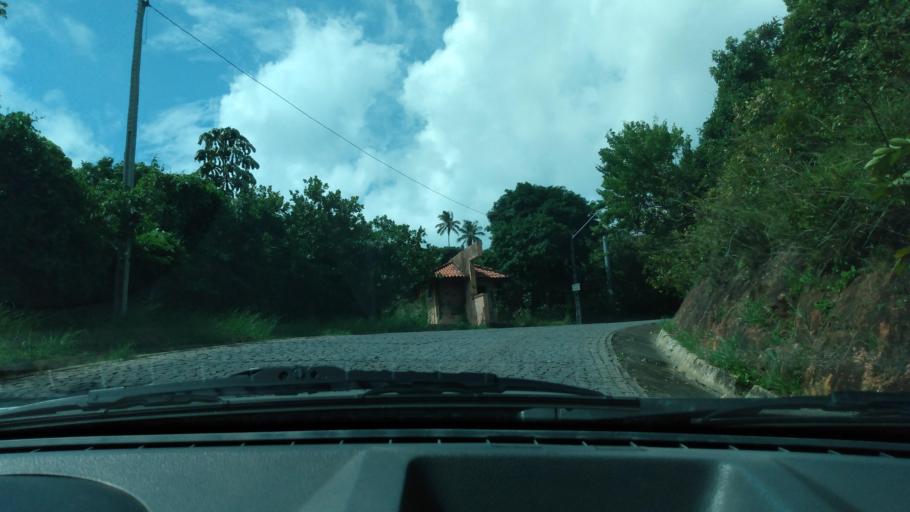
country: BR
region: Pernambuco
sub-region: Cabo De Santo Agostinho
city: Cabo
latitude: -8.3533
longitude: -34.9528
